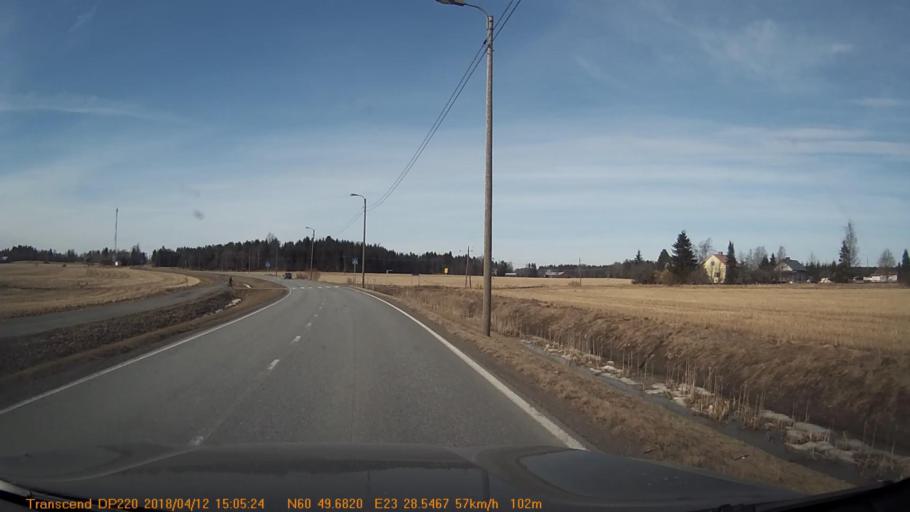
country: FI
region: Haeme
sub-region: Forssa
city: Jokioinen
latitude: 60.8282
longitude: 23.4757
